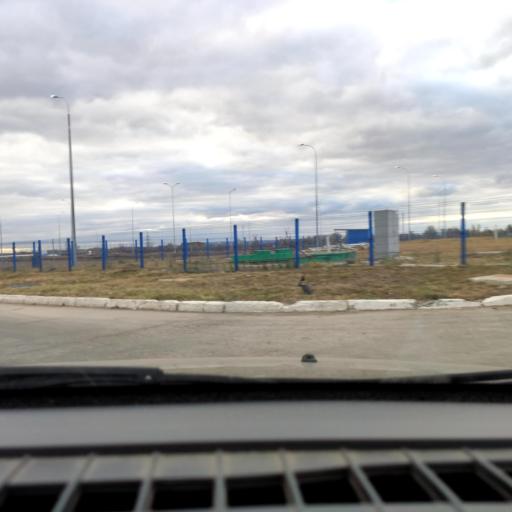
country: RU
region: Samara
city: Podstepki
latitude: 53.5554
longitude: 49.2141
